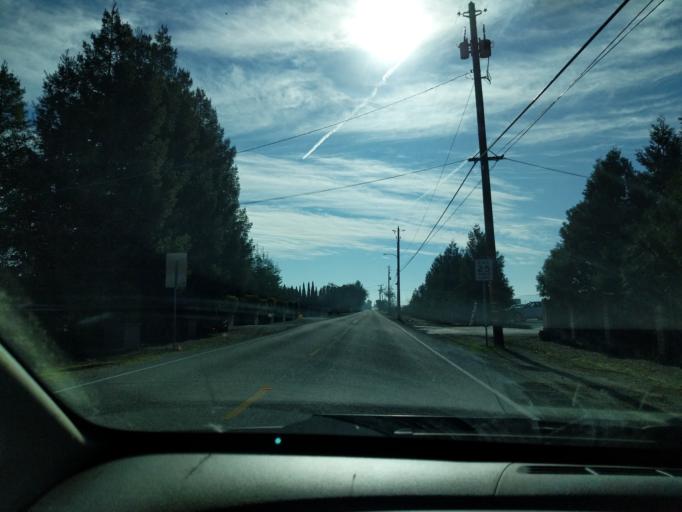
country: US
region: California
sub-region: Santa Clara County
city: San Martin
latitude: 37.0824
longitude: -121.6050
